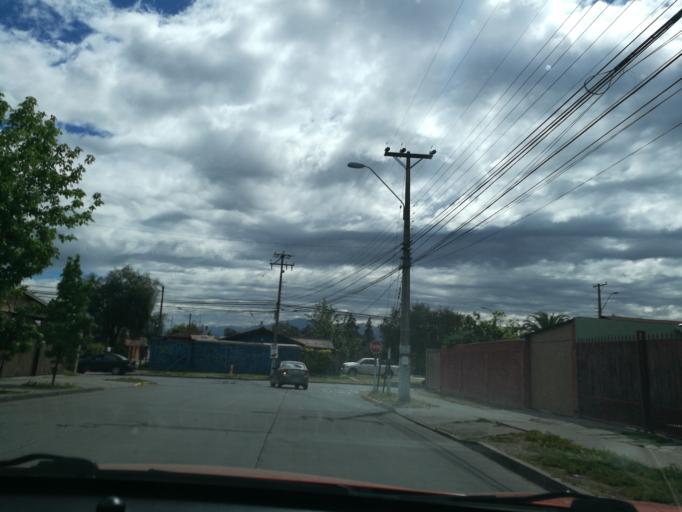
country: CL
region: O'Higgins
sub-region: Provincia de Cachapoal
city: Rancagua
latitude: -34.1335
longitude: -70.7362
